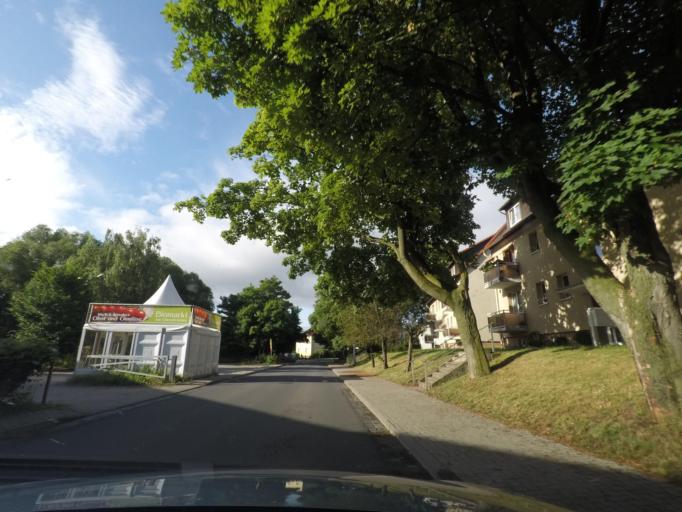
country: DE
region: Saxony-Anhalt
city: Derenburg
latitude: 51.8744
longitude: 10.9066
